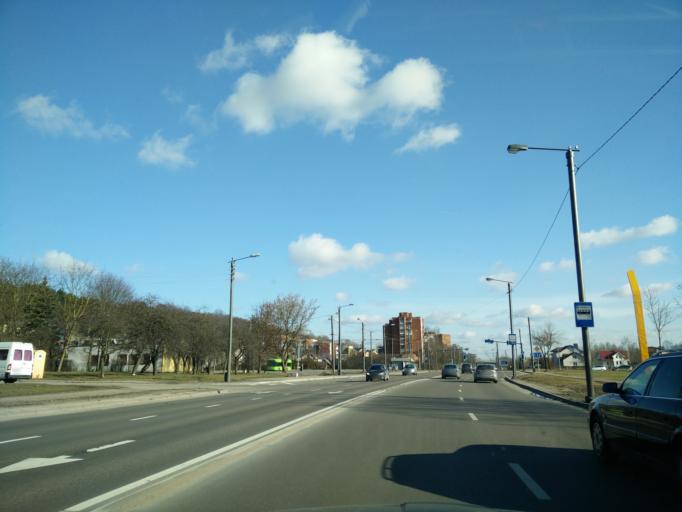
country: LT
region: Kauno apskritis
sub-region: Kauno rajonas
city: Akademija (Kaunas)
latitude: 54.9198
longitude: 23.8275
